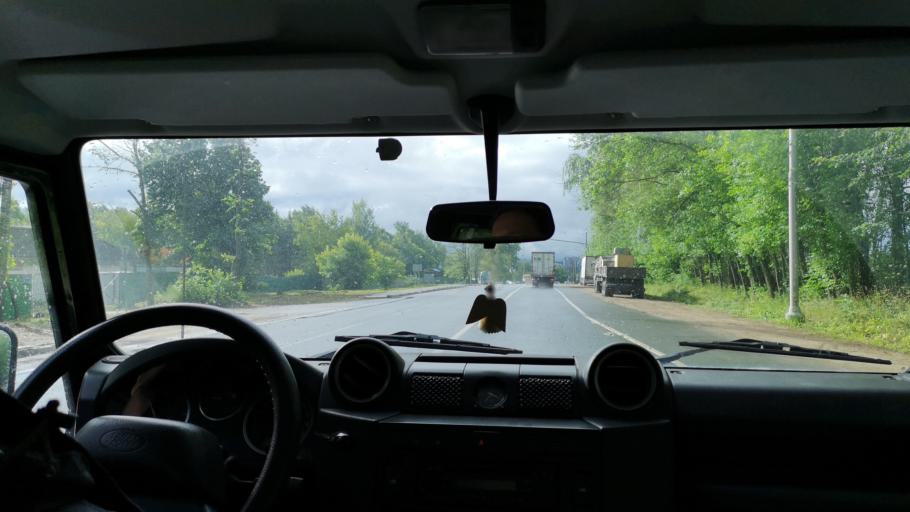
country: RU
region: Moskovskaya
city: Dmitrov
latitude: 56.3602
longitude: 37.4848
